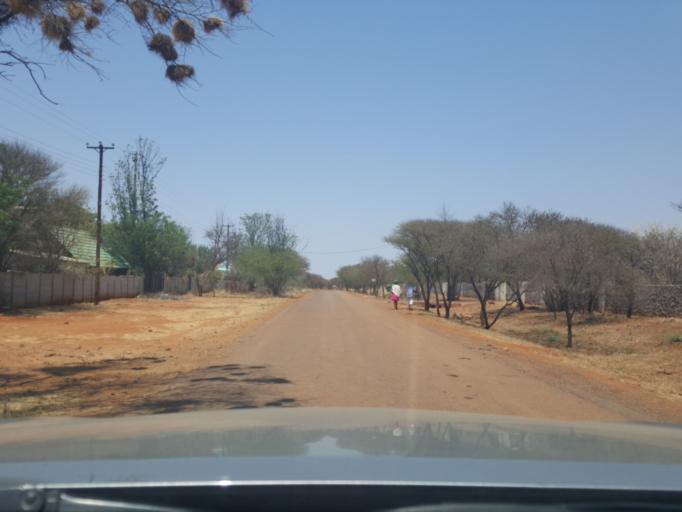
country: BW
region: South East
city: Ramotswa
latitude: -24.7713
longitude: 25.8452
